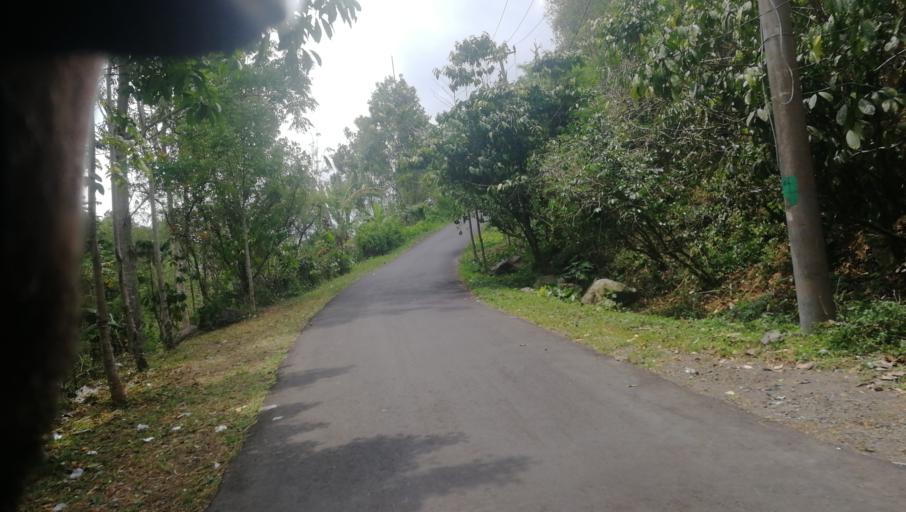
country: ID
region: Bali
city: Munduk
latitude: -8.2917
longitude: 115.0439
